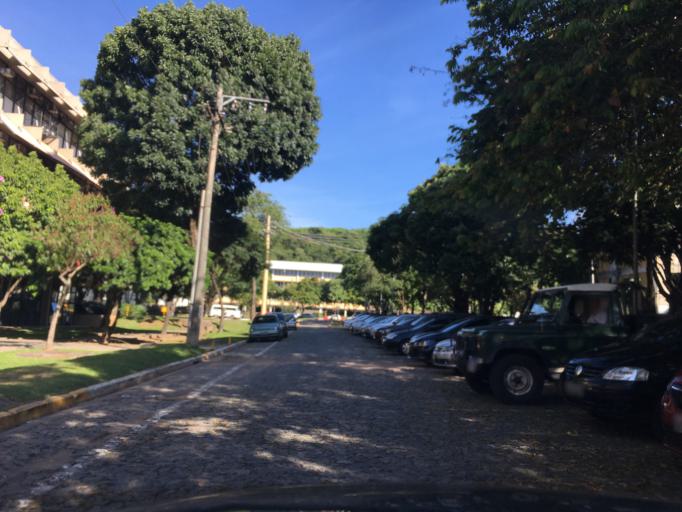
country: BR
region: Minas Gerais
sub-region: Belo Horizonte
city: Belo Horizonte
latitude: -19.8679
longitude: -43.9657
